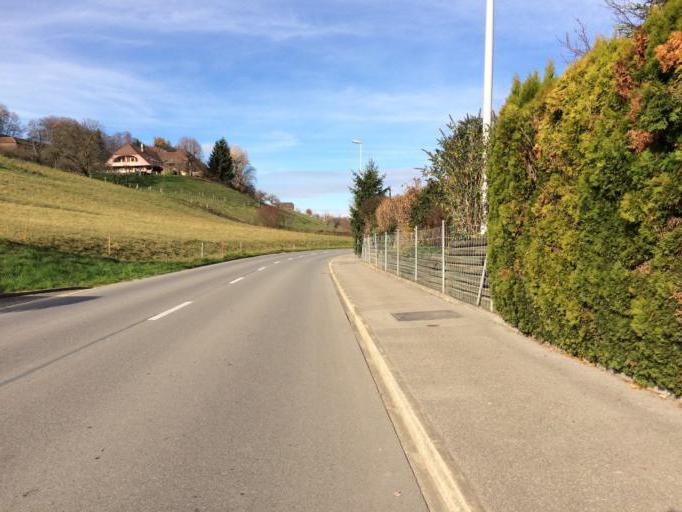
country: CH
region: Bern
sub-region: Bern-Mittelland District
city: Belp
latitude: 46.8990
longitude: 7.4876
